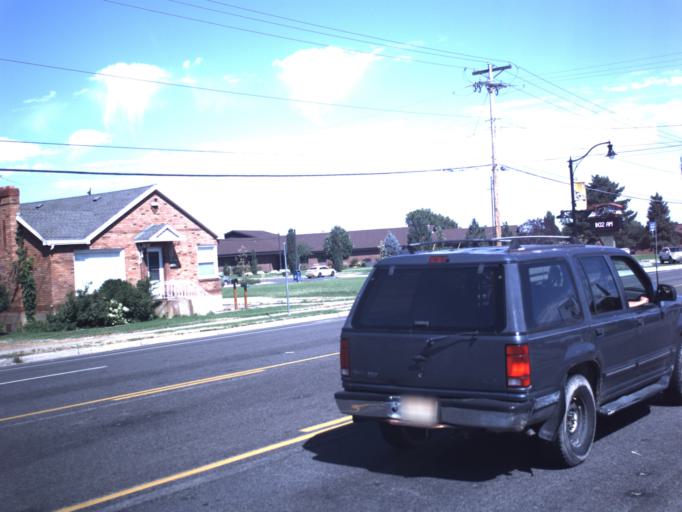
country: US
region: Utah
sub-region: Weber County
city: Roy
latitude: 41.1704
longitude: -112.0259
